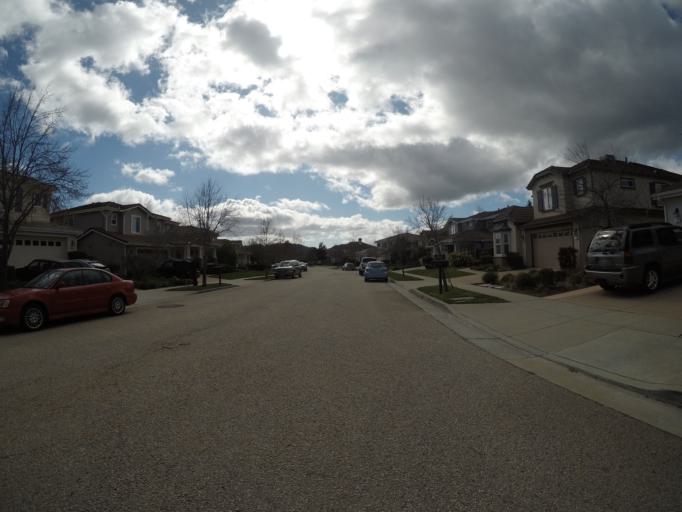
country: US
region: California
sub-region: Santa Cruz County
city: Scotts Valley
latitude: 37.0712
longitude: -122.0037
